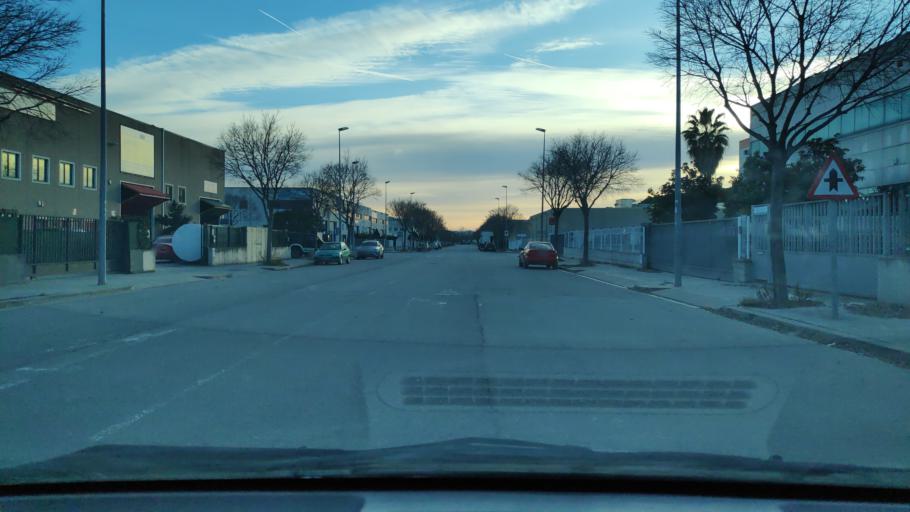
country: ES
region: Catalonia
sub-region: Provincia de Barcelona
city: Montmelo
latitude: 41.5702
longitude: 2.2670
